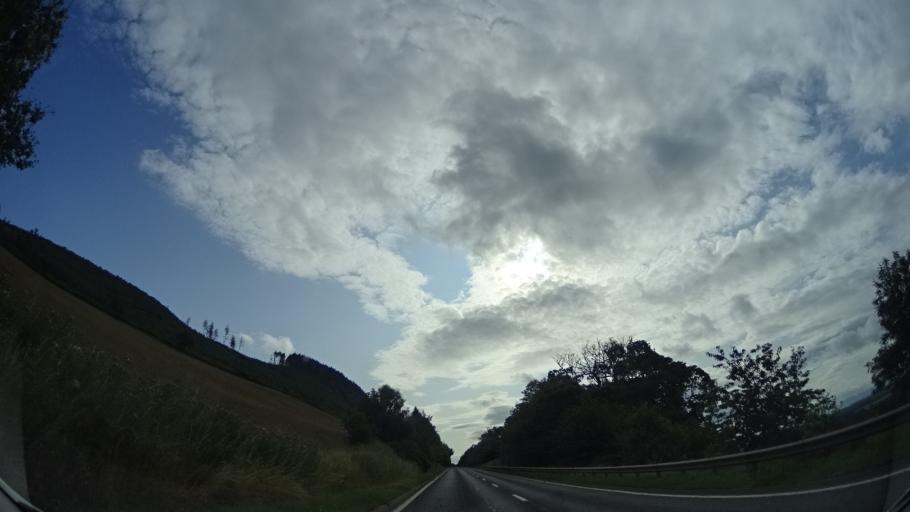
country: GB
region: Scotland
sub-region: Highland
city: Muir of Ord
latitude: 57.5586
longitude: -4.5275
